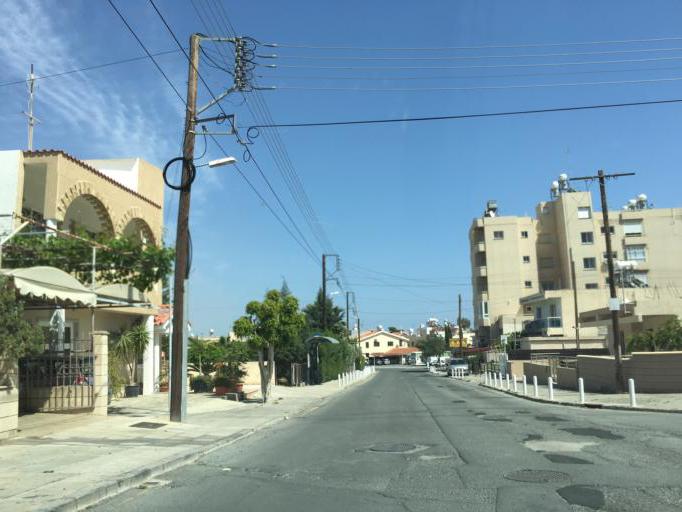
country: CY
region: Limassol
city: Mouttagiaka
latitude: 34.7034
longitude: 33.0829
